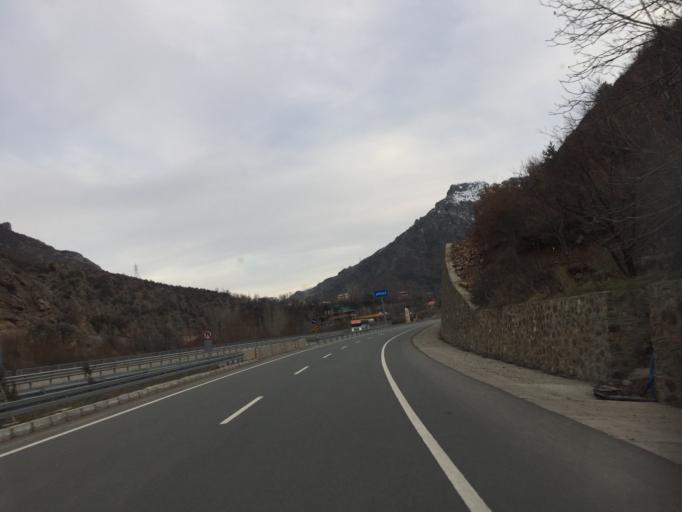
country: TR
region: Gumushane
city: Torul
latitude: 40.5459
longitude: 39.3231
